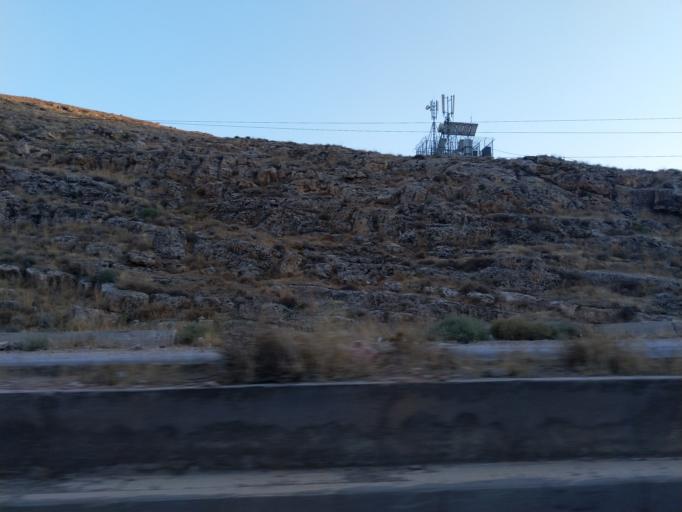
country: SY
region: Rif-dimashq
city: At Tall
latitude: 33.5672
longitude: 36.3066
